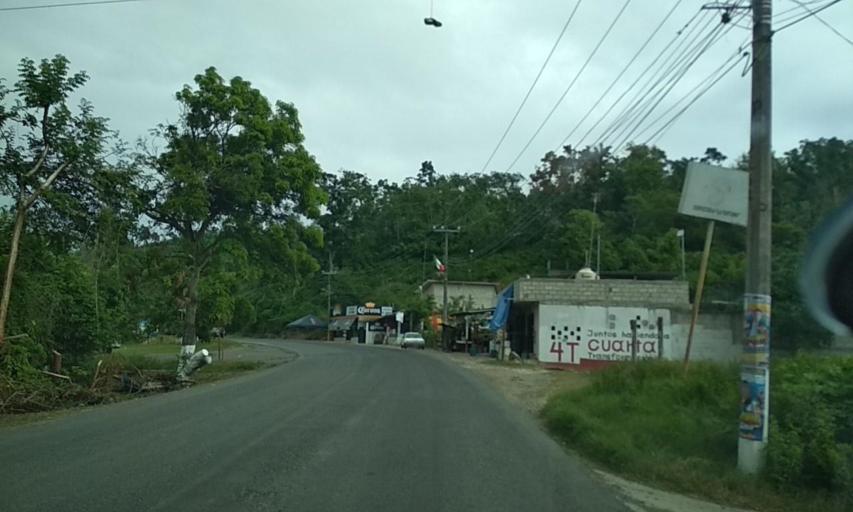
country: MX
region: Veracruz
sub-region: Papantla
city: Residencial Tajin
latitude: 20.6414
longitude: -97.3633
